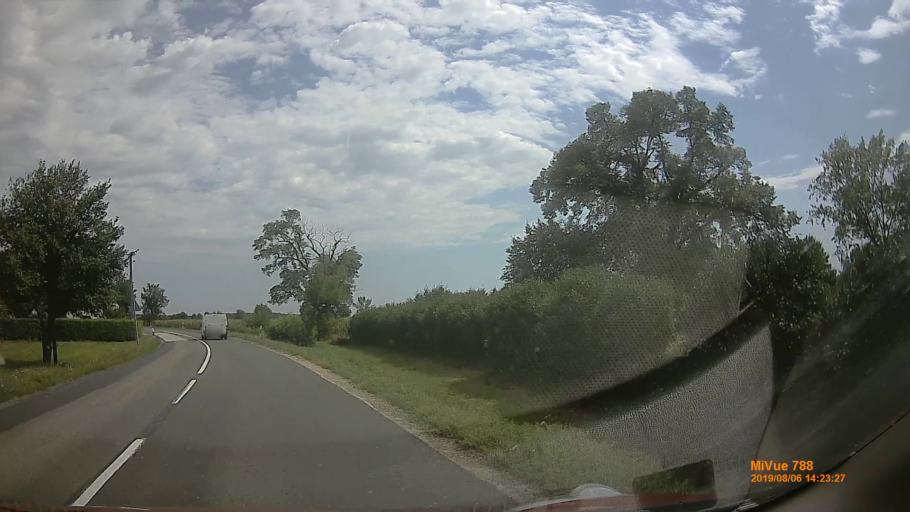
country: HU
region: Vas
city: Vasvar
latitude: 47.1539
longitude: 16.8049
